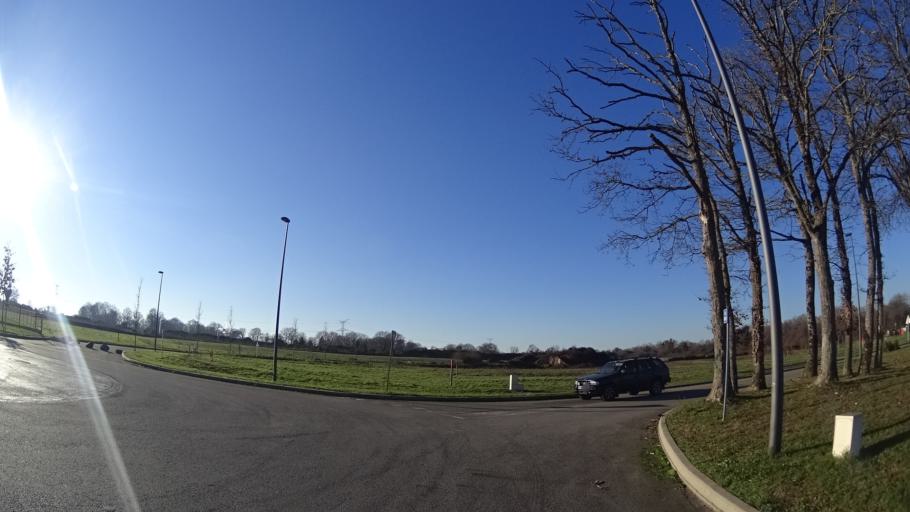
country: FR
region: Brittany
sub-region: Departement du Morbihan
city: Allaire
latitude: 47.6337
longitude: -2.1772
